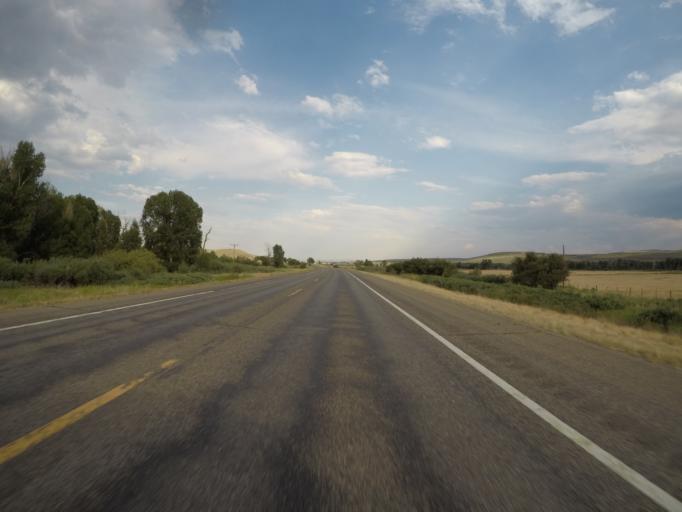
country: US
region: Colorado
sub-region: Moffat County
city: Craig
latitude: 40.5301
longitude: -107.4349
